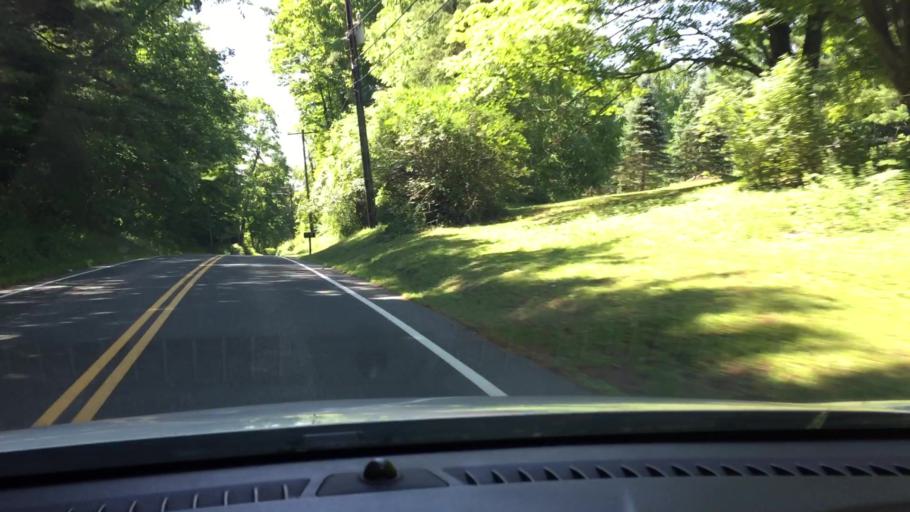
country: US
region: Massachusetts
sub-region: Berkshire County
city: Lenox
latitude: 42.3852
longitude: -73.2566
